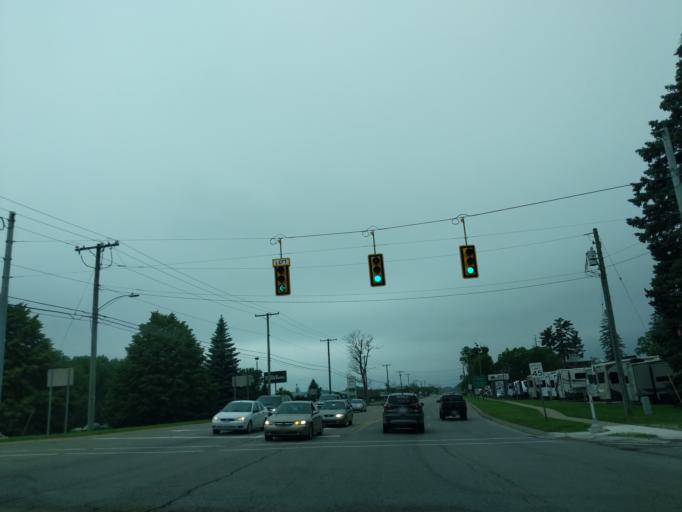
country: US
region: Michigan
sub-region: Branch County
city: Coldwater
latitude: 41.9343
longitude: -84.9614
